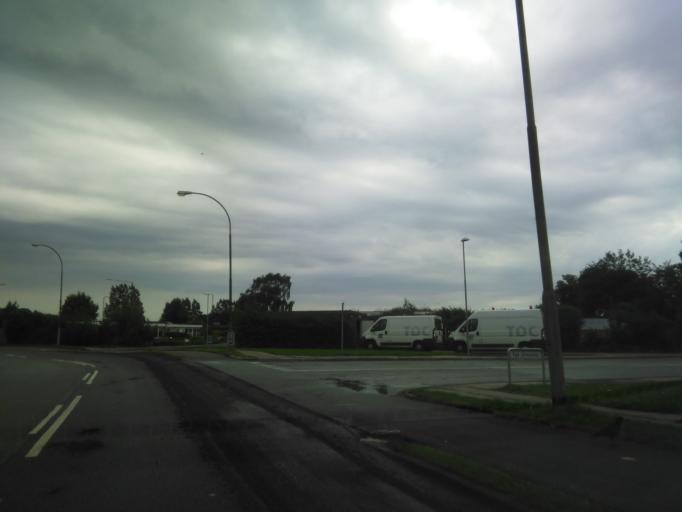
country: DK
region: Central Jutland
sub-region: Arhus Kommune
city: Hjortshoj
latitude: 56.2072
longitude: 10.2711
